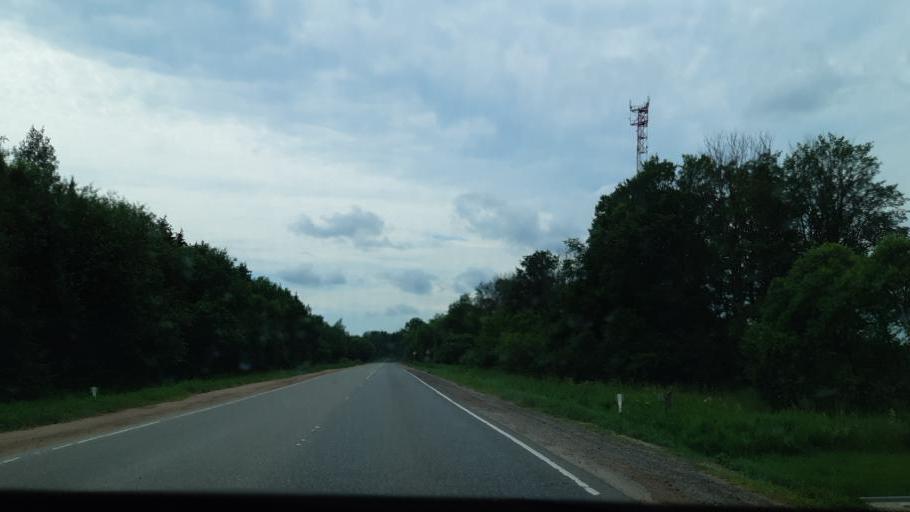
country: RU
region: Moskovskaya
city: Vereya
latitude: 55.3836
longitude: 36.3033
